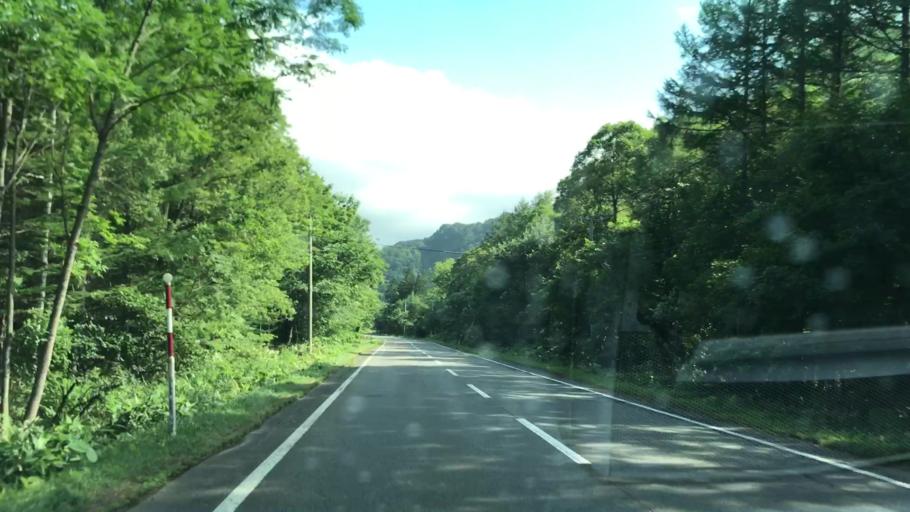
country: JP
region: Hokkaido
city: Shizunai-furukawacho
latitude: 42.8278
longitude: 142.4163
